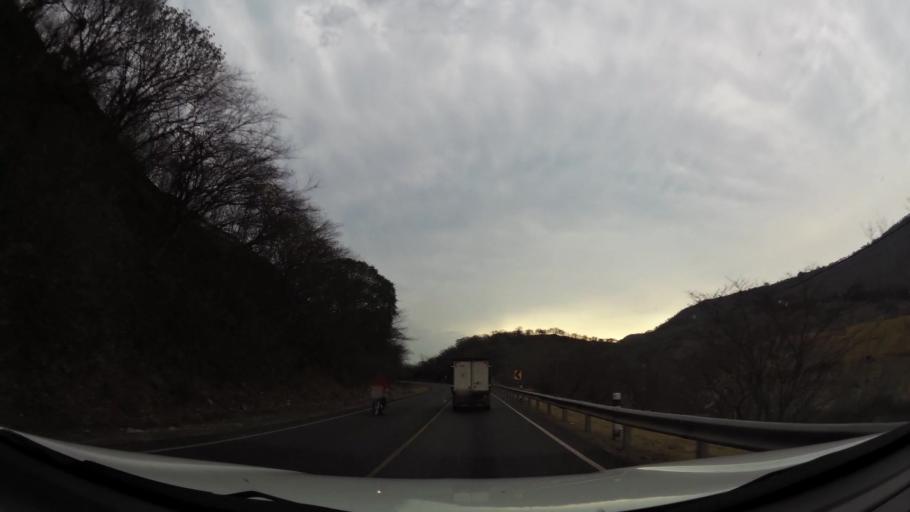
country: NI
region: Esteli
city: Esteli
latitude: 12.9426
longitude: -86.2180
